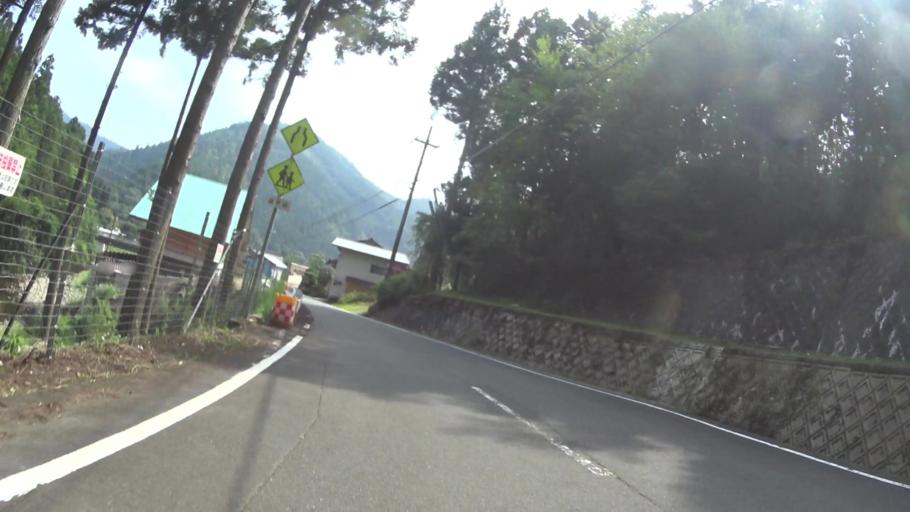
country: JP
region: Fukui
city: Obama
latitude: 35.3149
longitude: 135.6414
